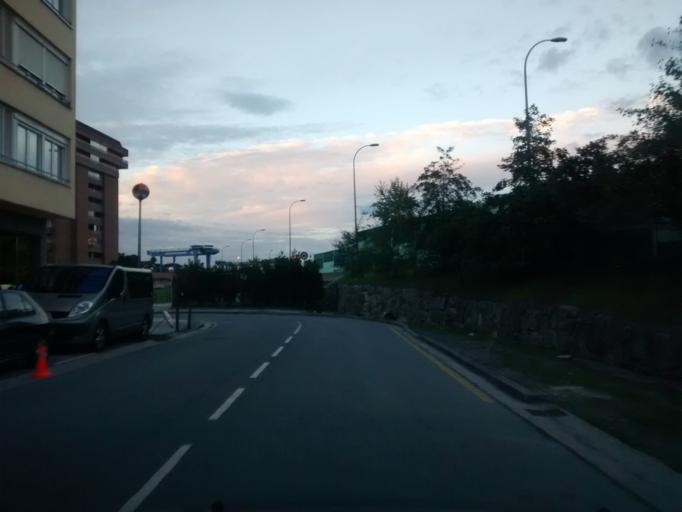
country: ES
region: Basque Country
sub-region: Provincia de Guipuzcoa
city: Zumaia
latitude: 43.2921
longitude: -2.2534
